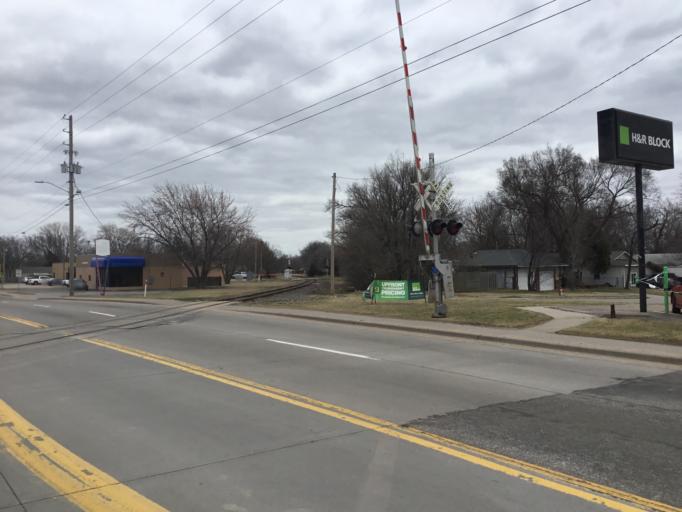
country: US
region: Kansas
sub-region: Sedgwick County
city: Wichita
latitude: 37.6949
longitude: -97.3795
